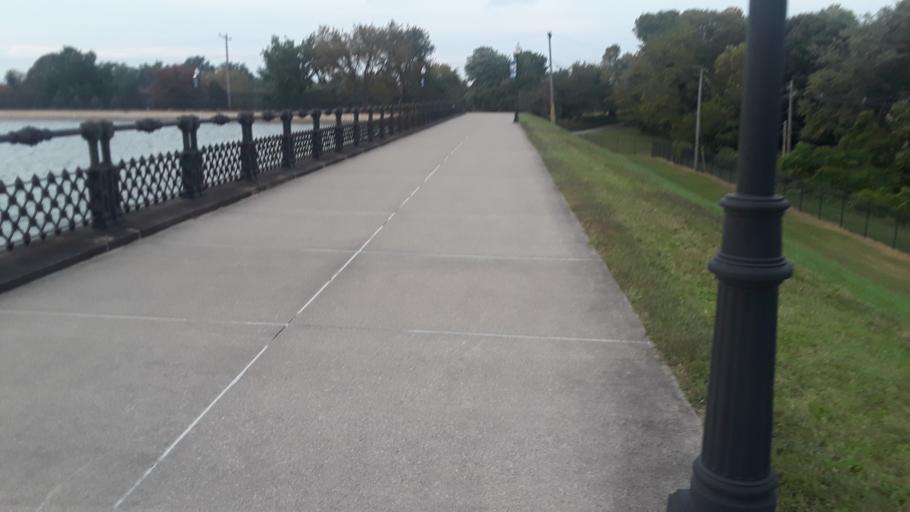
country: US
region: Kentucky
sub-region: Jefferson County
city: Indian Hills
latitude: 38.2578
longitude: -85.6780
